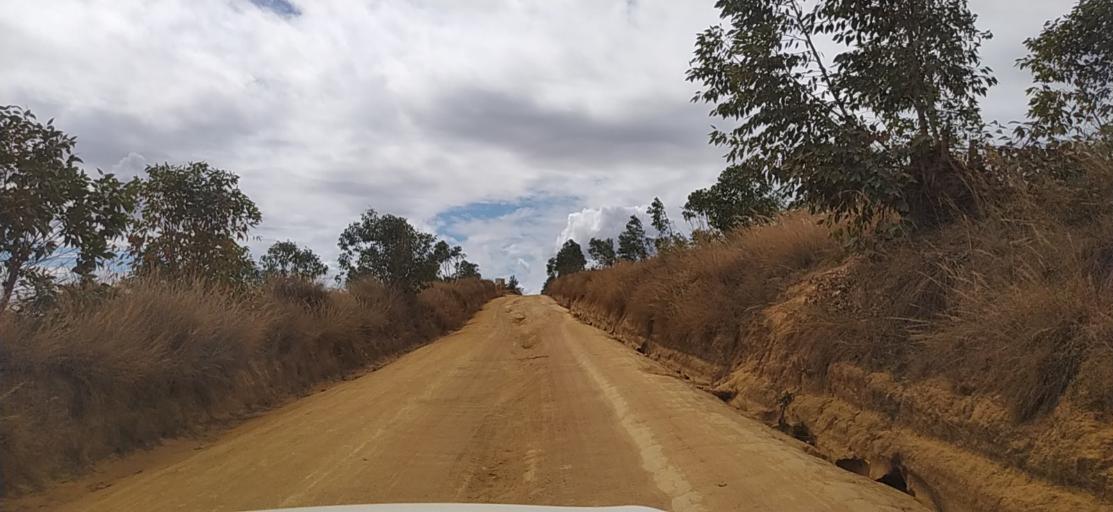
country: MG
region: Alaotra Mangoro
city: Ambatondrazaka
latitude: -17.9492
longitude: 48.2490
